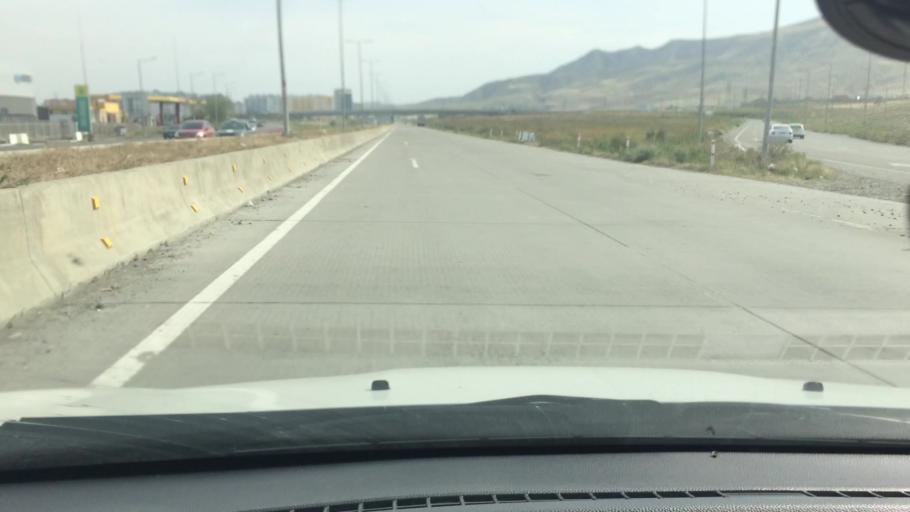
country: GE
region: Kvemo Kartli
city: Rust'avi
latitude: 41.5749
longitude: 44.9573
